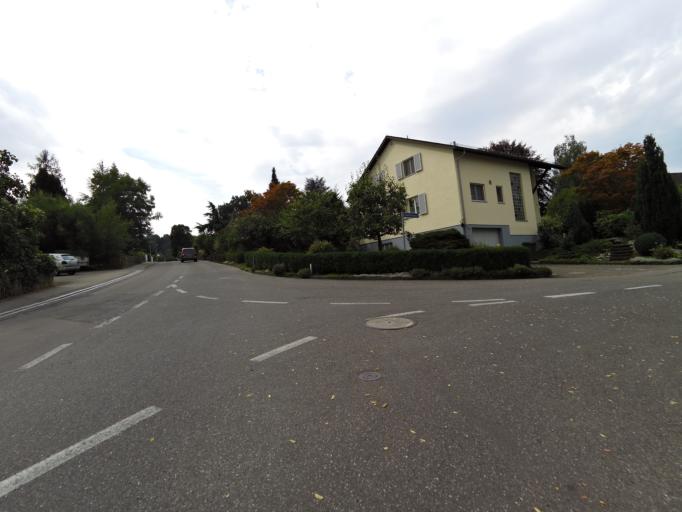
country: CH
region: Thurgau
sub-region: Kreuzlingen District
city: Tagerwilen
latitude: 47.6528
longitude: 9.1294
